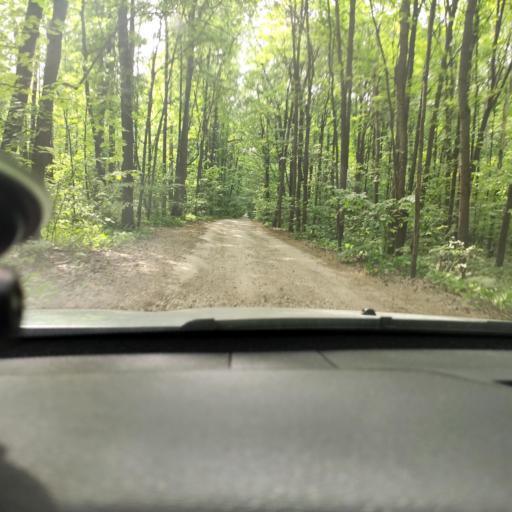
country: RU
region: Samara
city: Novosemeykino
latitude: 53.3273
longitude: 50.2231
